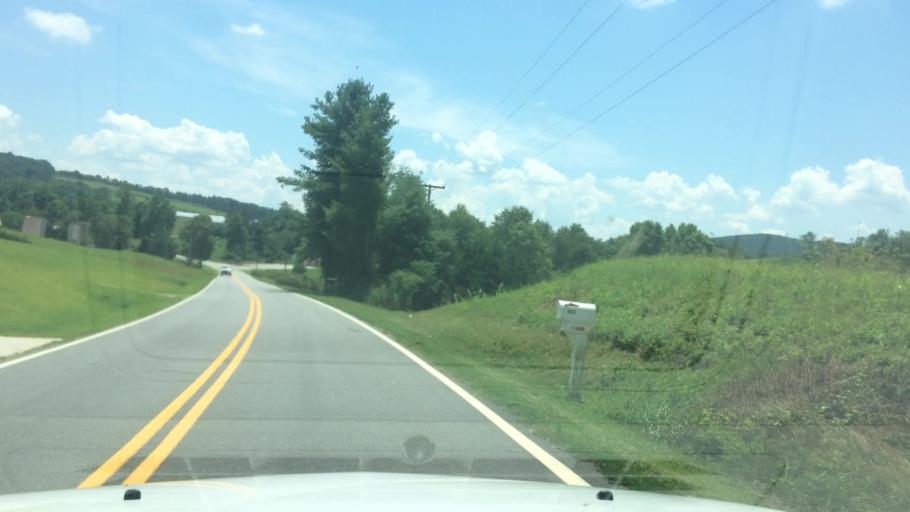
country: US
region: North Carolina
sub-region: Alexander County
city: Taylorsville
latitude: 35.9350
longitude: -81.2670
